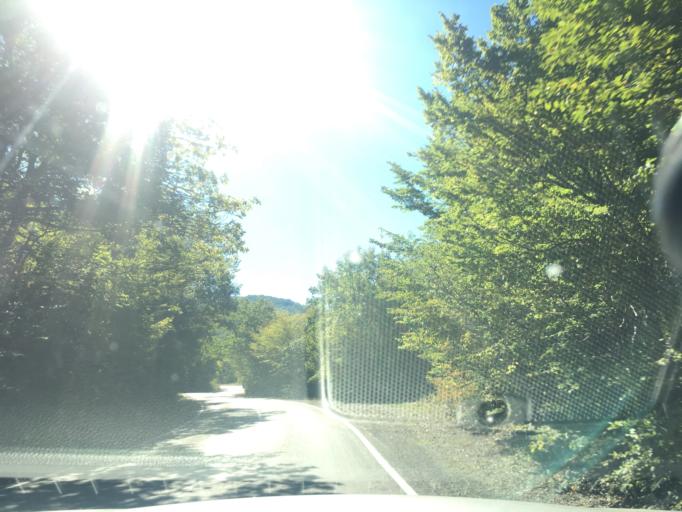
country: GE
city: Didi Lilo
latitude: 41.8648
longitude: 44.9107
